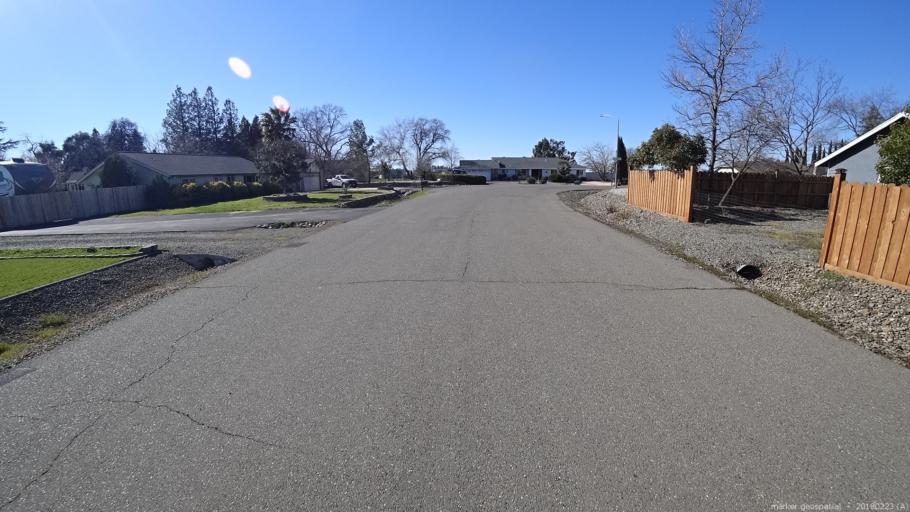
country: US
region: California
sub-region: Sacramento County
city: Rio Linda
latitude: 38.7066
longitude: -121.4190
